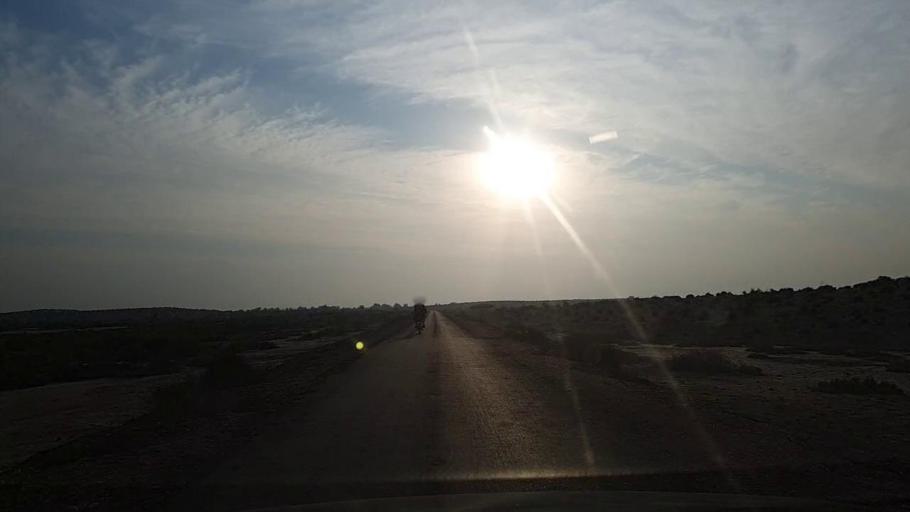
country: PK
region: Sindh
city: Jam Sahib
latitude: 26.4150
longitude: 68.5161
